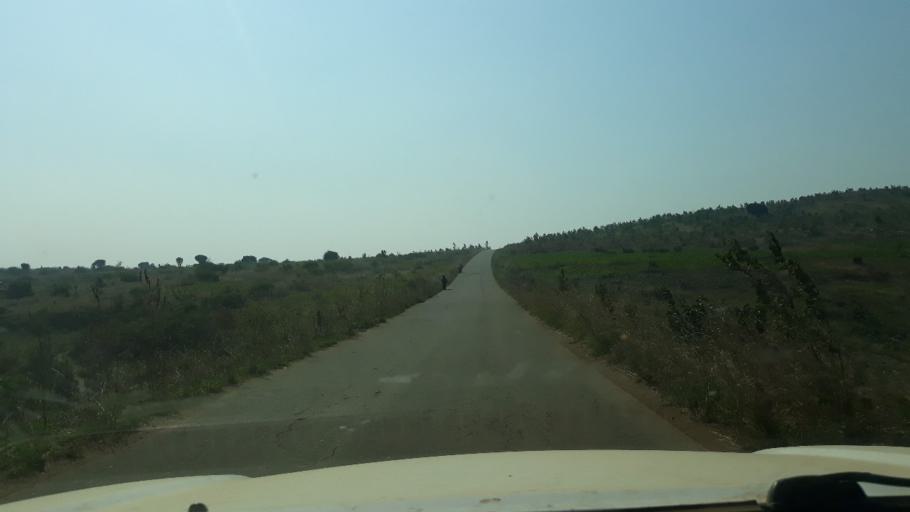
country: BI
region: Cibitoke
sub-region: Commune of Buganda
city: Buganda
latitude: -3.0129
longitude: 29.1036
